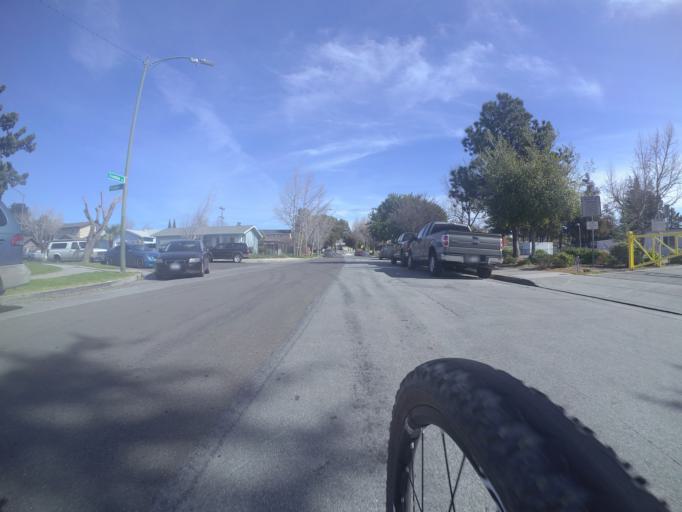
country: US
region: California
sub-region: Santa Clara County
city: Milpitas
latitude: 37.4094
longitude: -121.8812
